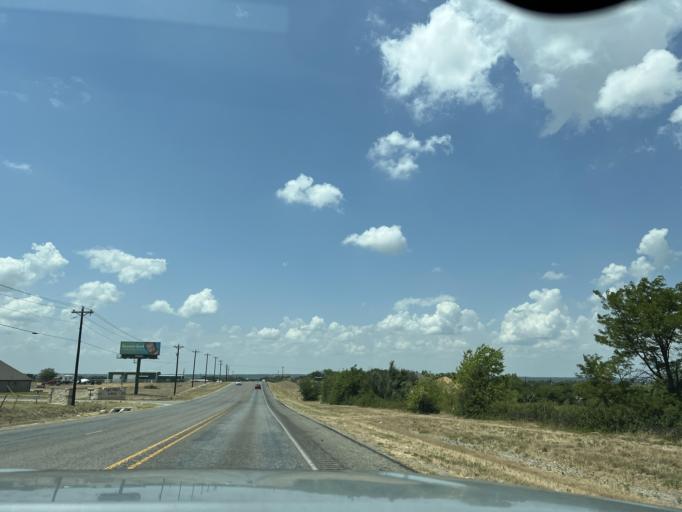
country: US
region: Texas
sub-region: Parker County
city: Springtown
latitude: 32.9035
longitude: -97.7248
